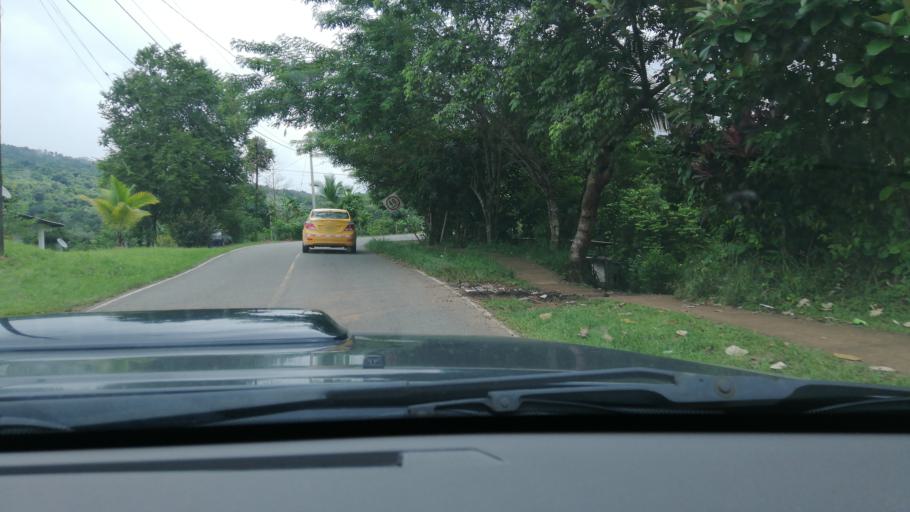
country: PA
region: Panama
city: Cerro Azul
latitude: 9.1095
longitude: -79.4451
